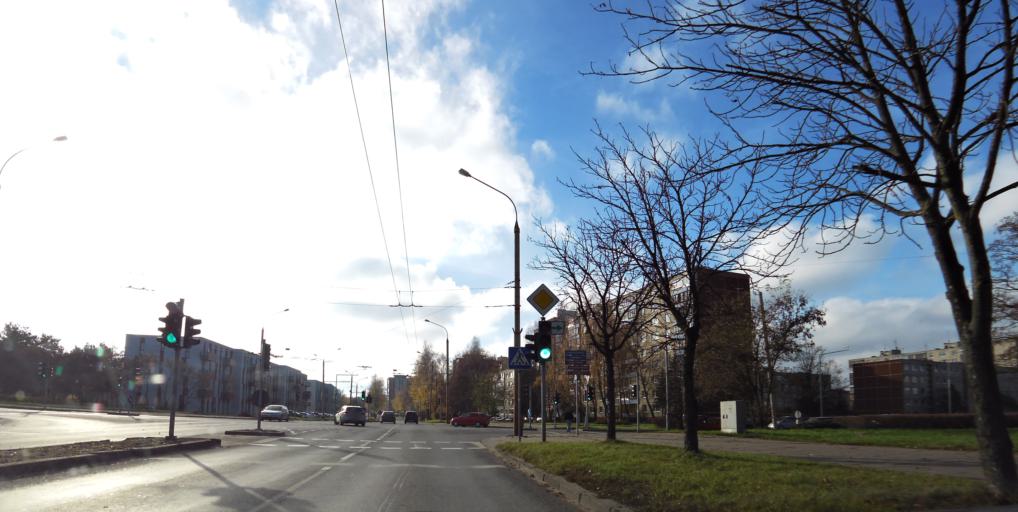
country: LT
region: Vilnius County
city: Lazdynai
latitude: 54.6886
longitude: 25.2080
